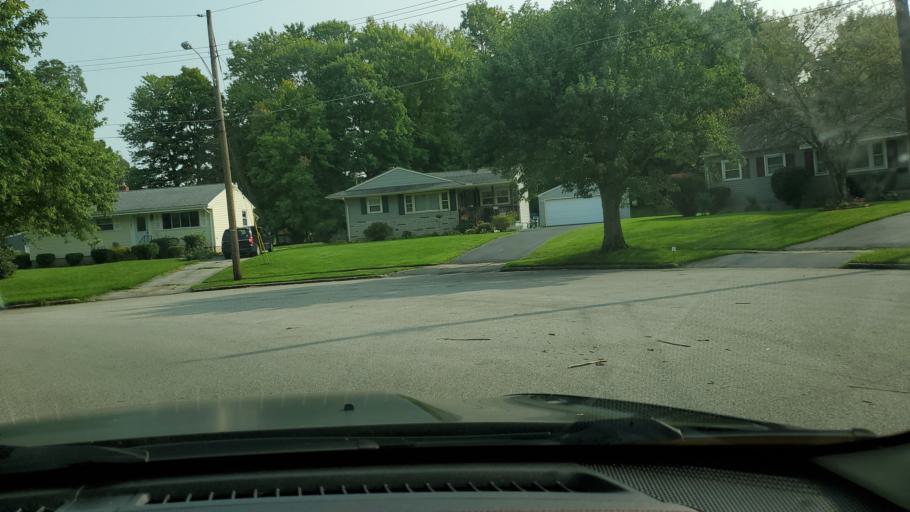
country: US
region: Ohio
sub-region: Mahoning County
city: Poland
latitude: 41.0372
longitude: -80.6305
